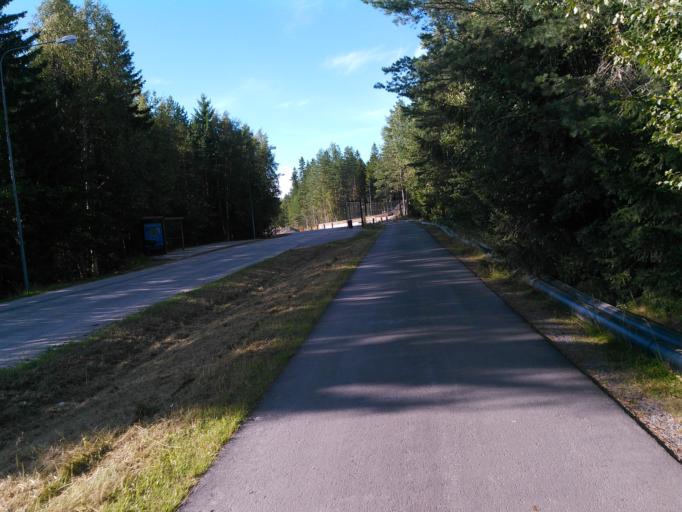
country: SE
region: Vaesterbotten
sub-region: Umea Kommun
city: Ersmark
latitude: 63.8279
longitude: 20.3245
